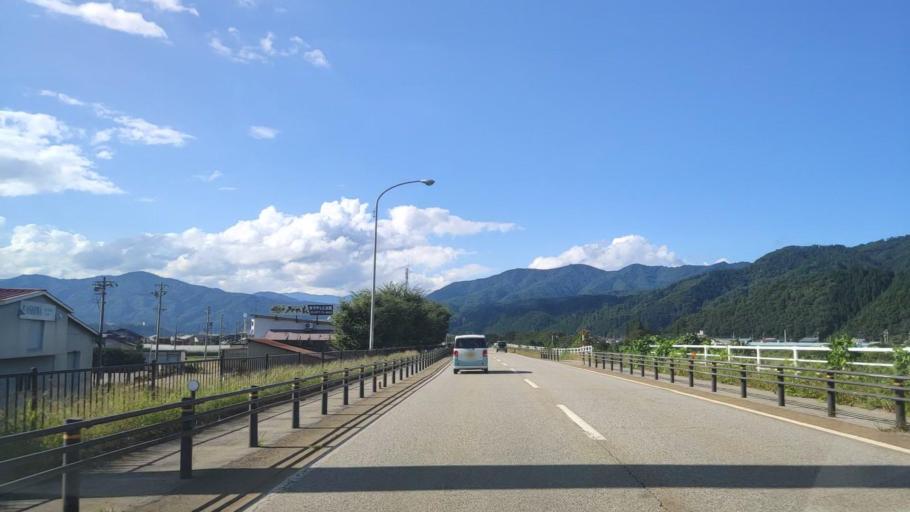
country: JP
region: Gifu
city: Takayama
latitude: 36.2426
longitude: 137.1726
